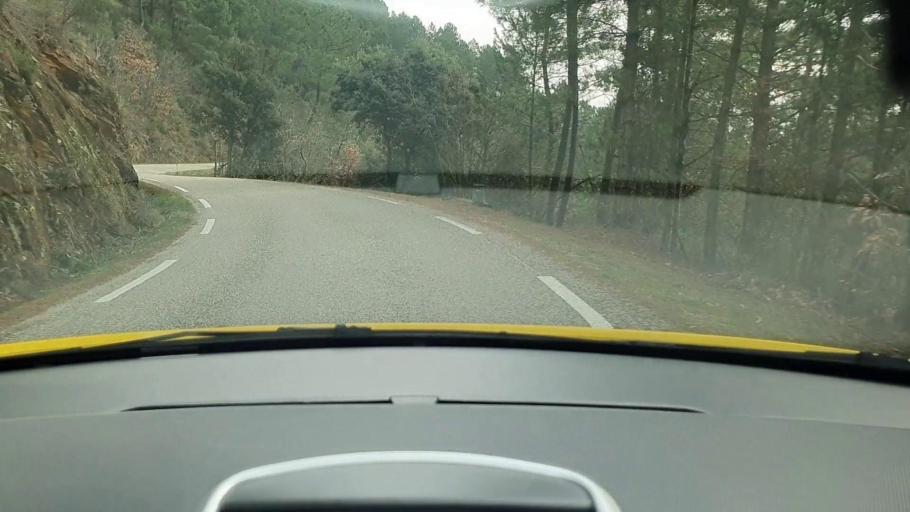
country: FR
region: Languedoc-Roussillon
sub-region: Departement du Gard
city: Besseges
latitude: 44.3250
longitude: 4.0703
